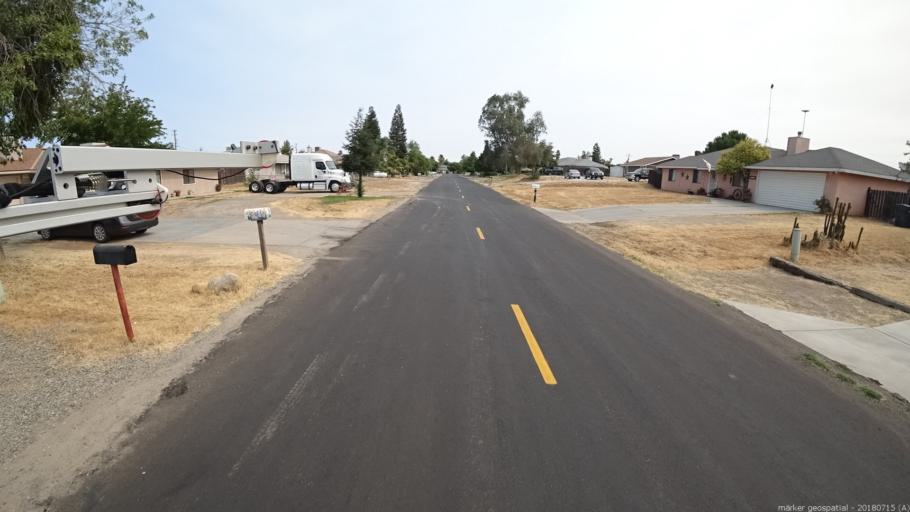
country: US
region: California
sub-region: Madera County
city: Madera Acres
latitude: 37.0155
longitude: -120.0719
